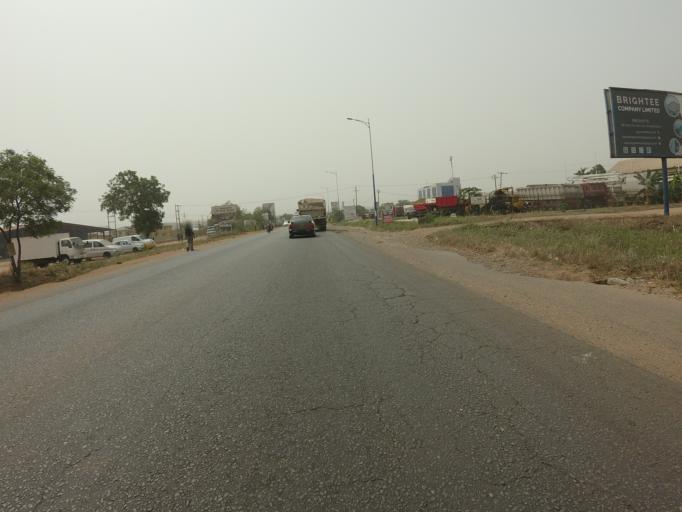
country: GH
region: Greater Accra
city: Tema
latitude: 5.7232
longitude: 0.0206
